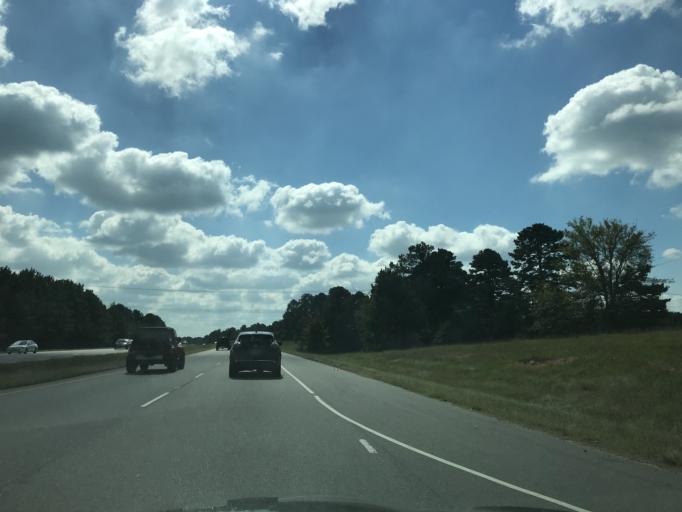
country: US
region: North Carolina
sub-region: Wake County
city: Wake Forest
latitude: 35.9376
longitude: -78.5420
